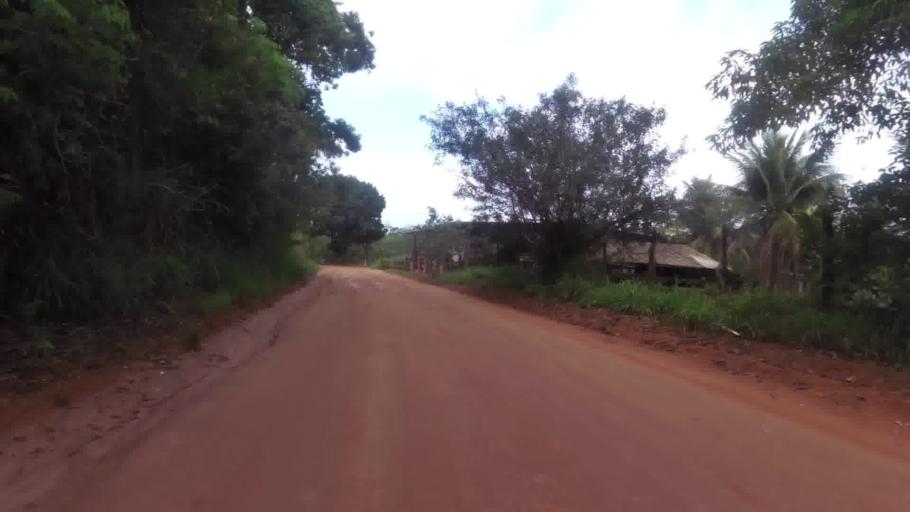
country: BR
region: Espirito Santo
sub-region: Piuma
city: Piuma
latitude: -20.7888
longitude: -40.6333
